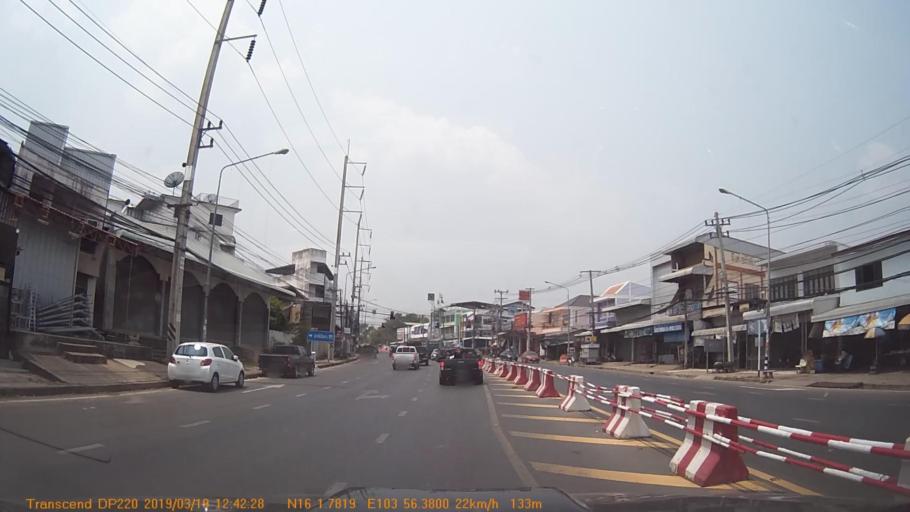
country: TH
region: Roi Et
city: Selaphum
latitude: 16.0298
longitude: 103.9396
